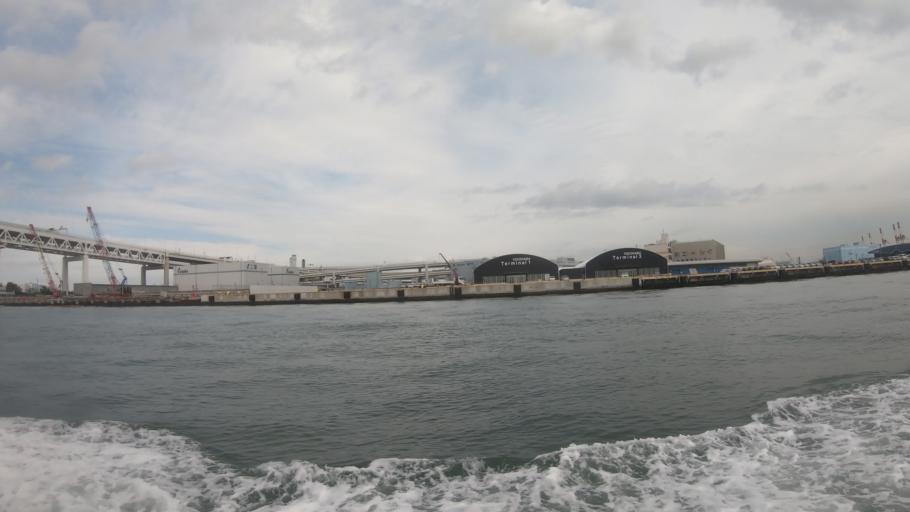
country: JP
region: Kanagawa
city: Yokohama
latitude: 35.4559
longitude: 139.6796
